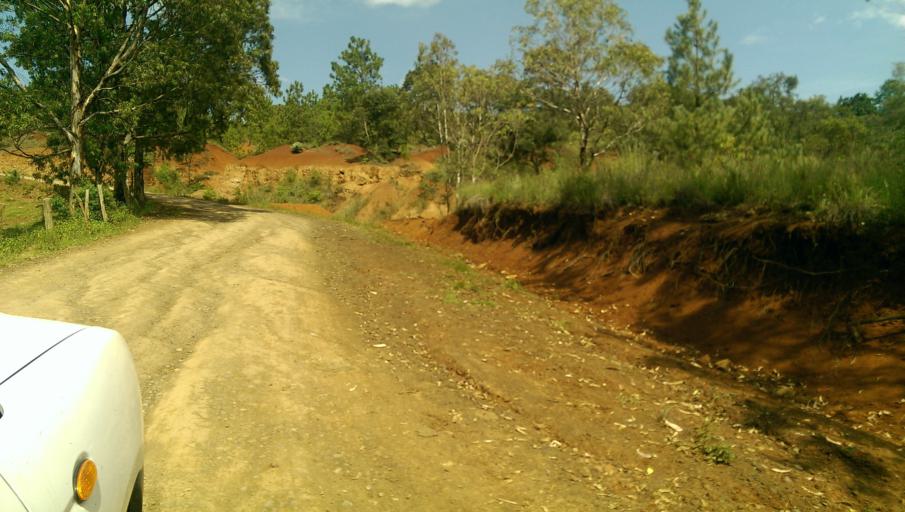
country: MX
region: Michoacan
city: Acuitzio del Canje
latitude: 19.4715
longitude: -101.3647
